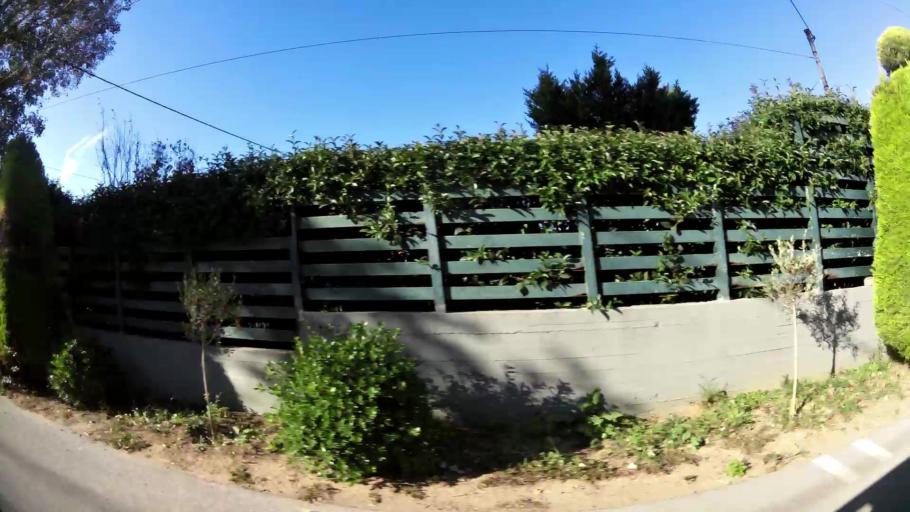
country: GR
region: Attica
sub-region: Nomarchia Anatolikis Attikis
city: Anoixi
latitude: 38.1298
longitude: 23.8499
